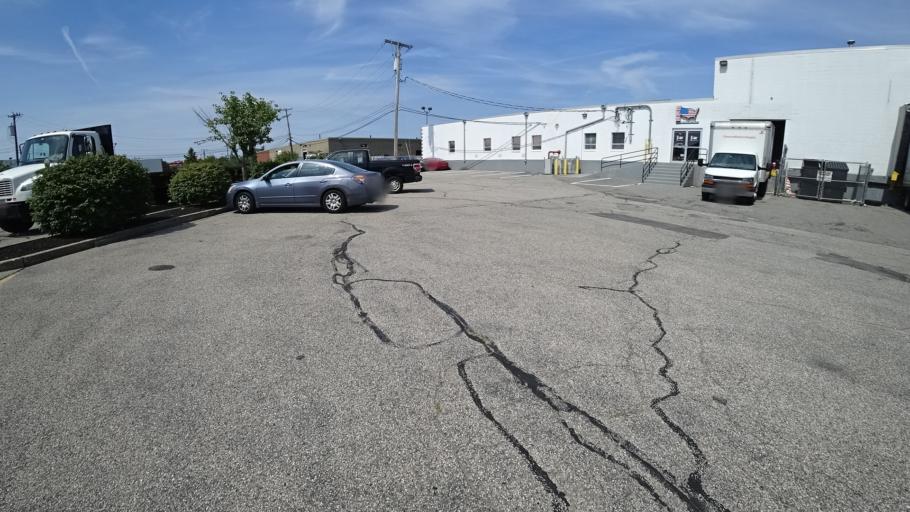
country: US
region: Massachusetts
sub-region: Norfolk County
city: Dedham
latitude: 42.2355
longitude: -71.1757
